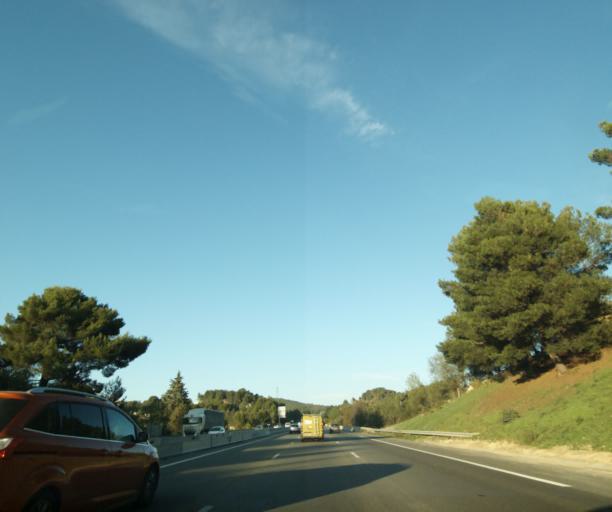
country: FR
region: Provence-Alpes-Cote d'Azur
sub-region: Departement des Bouches-du-Rhone
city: Roquevaire
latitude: 43.3366
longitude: 5.6072
